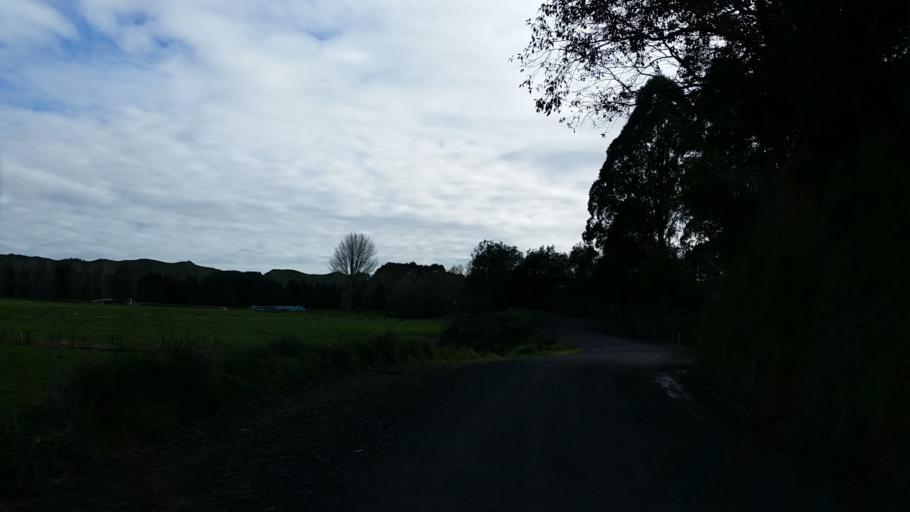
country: NZ
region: Taranaki
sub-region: South Taranaki District
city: Eltham
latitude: -39.2556
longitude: 174.5105
